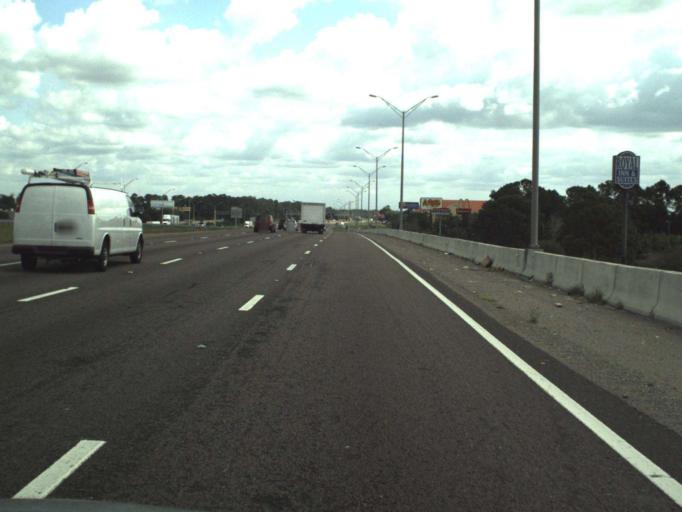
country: US
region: Florida
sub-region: Seminole County
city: Lake Mary
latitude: 28.8117
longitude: -81.3374
